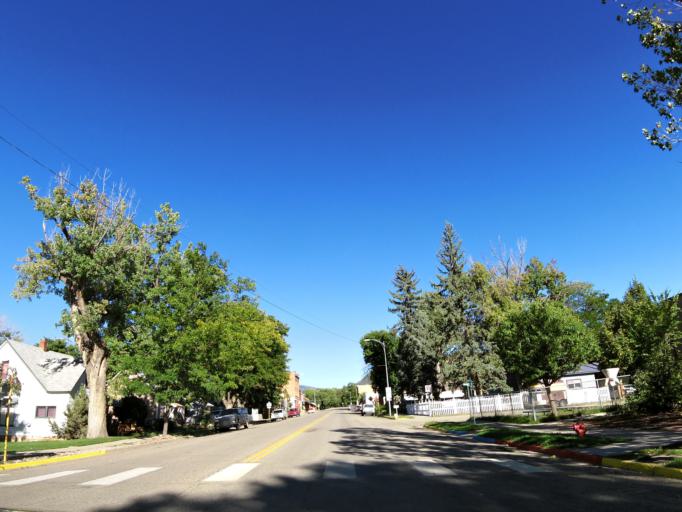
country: US
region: Colorado
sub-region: Montezuma County
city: Mancos
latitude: 37.3451
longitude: -108.2918
